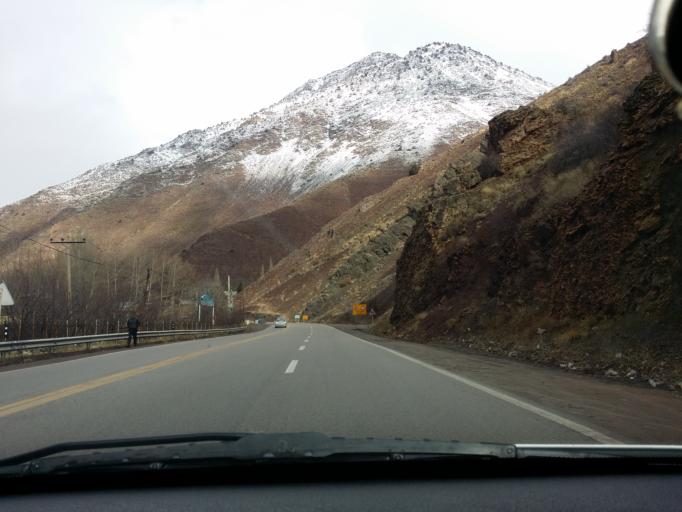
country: IR
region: Tehran
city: Tajrish
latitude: 36.0497
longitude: 51.3142
